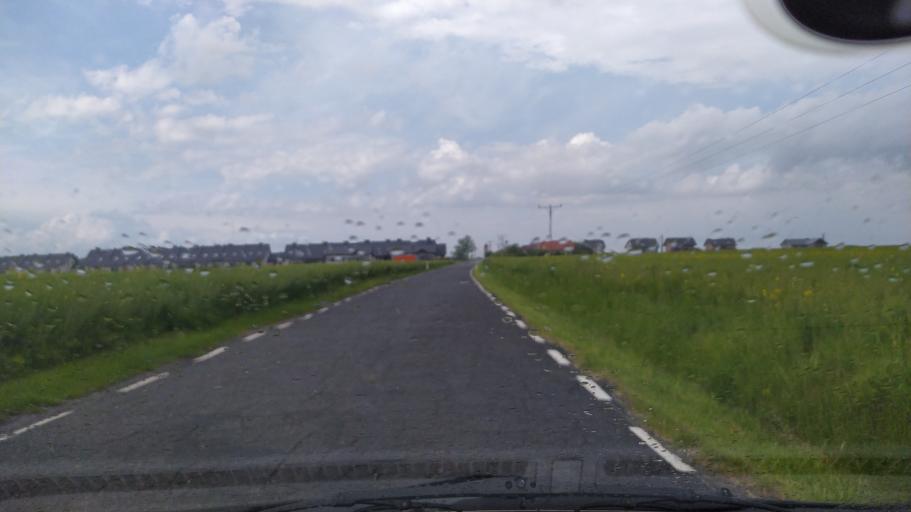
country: PL
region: Silesian Voivodeship
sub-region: Powiat gliwicki
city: Zernica
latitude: 50.2329
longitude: 18.6172
